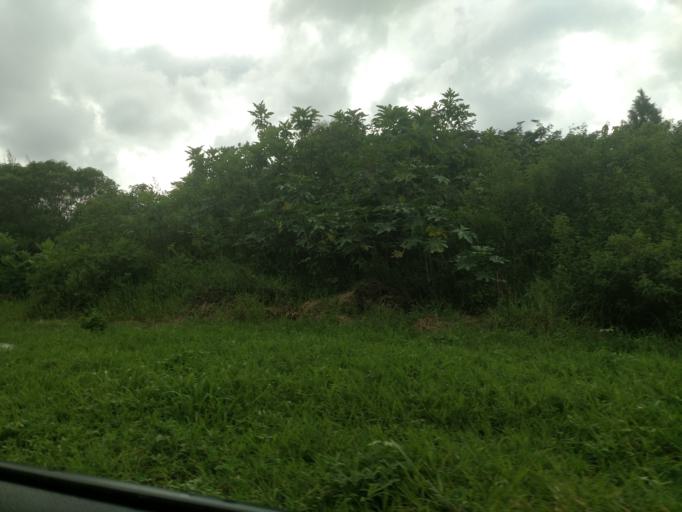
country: MX
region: Nayarit
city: Tepic
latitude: 21.4790
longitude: -104.8579
